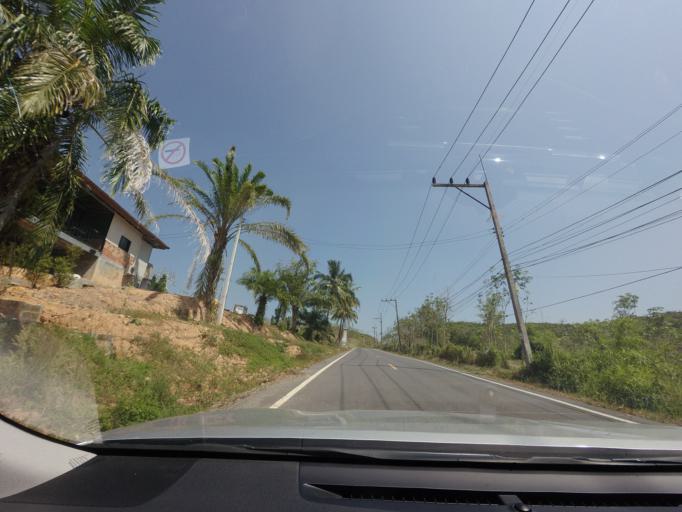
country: TH
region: Phangnga
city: Takua Thung
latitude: 8.2527
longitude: 98.4054
